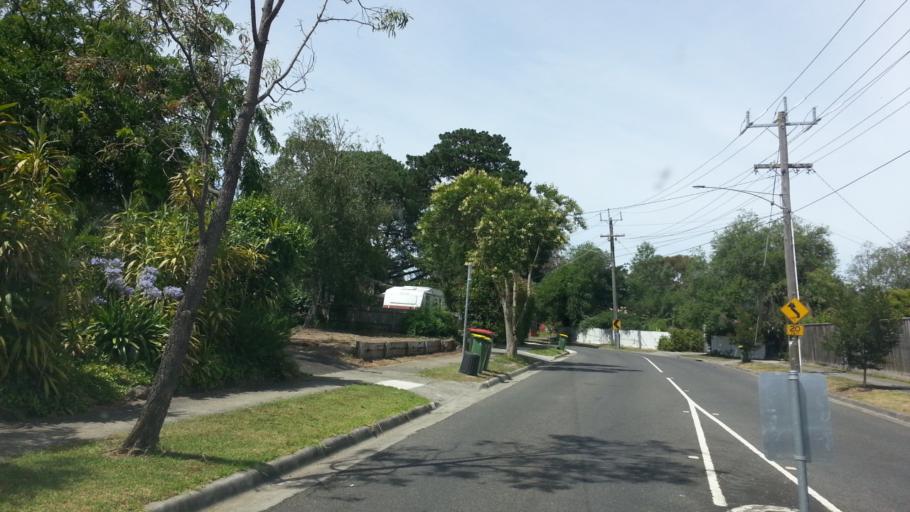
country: AU
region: Victoria
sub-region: Knox
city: Boronia
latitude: -37.8699
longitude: 145.2709
